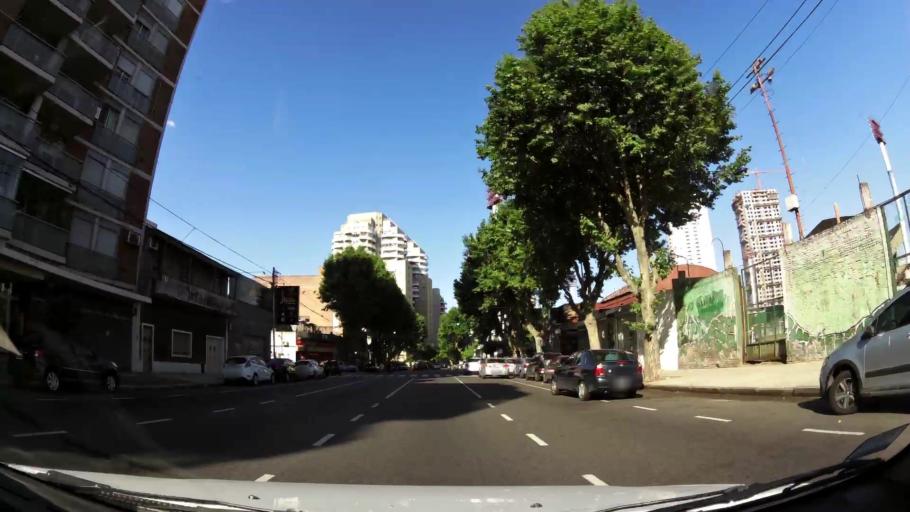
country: AR
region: Buenos Aires F.D.
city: Villa Santa Rita
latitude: -34.6185
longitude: -58.4494
